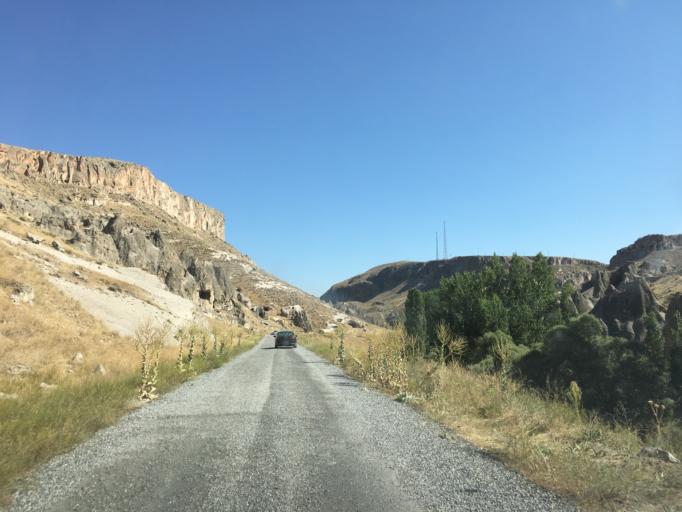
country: TR
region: Kayseri
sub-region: Yesilhisar
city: Yesilhisar
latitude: 38.3494
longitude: 34.9686
